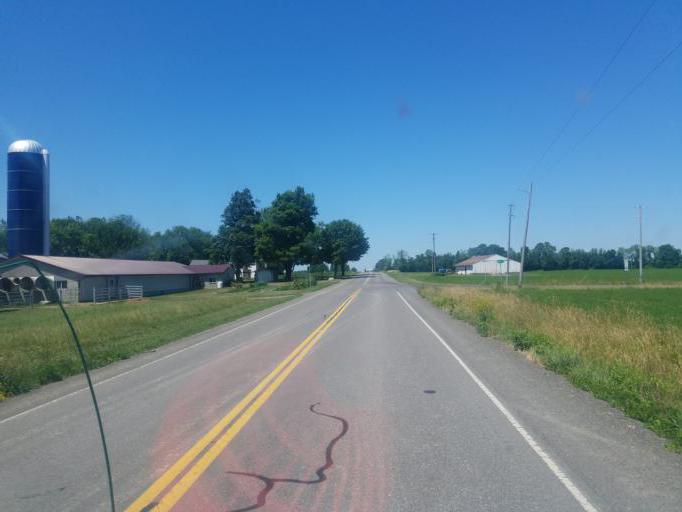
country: US
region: New York
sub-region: Yates County
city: Penn Yan
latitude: 42.7144
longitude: -76.9973
